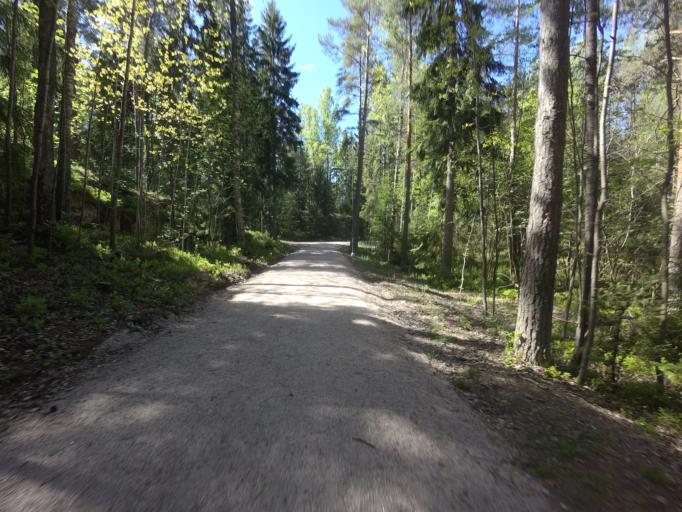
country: FI
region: Uusimaa
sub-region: Helsinki
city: Kauniainen
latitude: 60.1820
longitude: 24.7351
